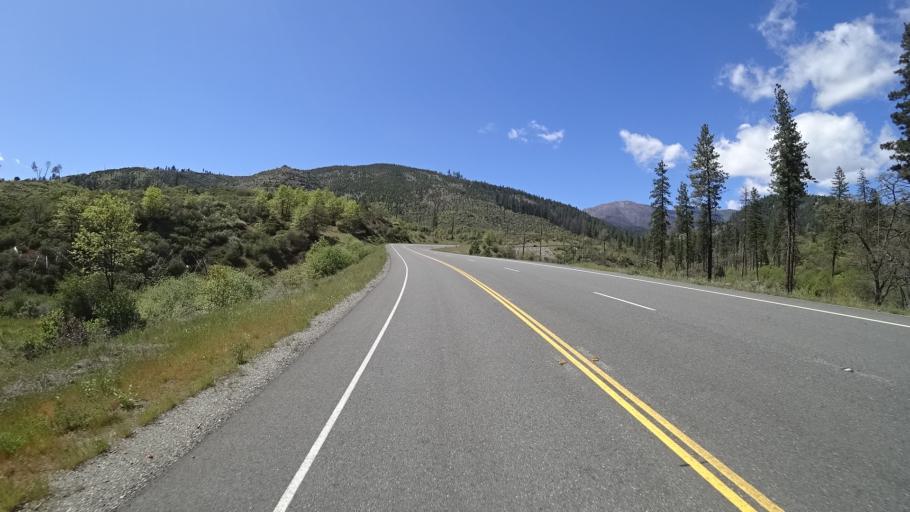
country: US
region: California
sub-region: Trinity County
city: Weaverville
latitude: 40.7431
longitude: -122.9692
